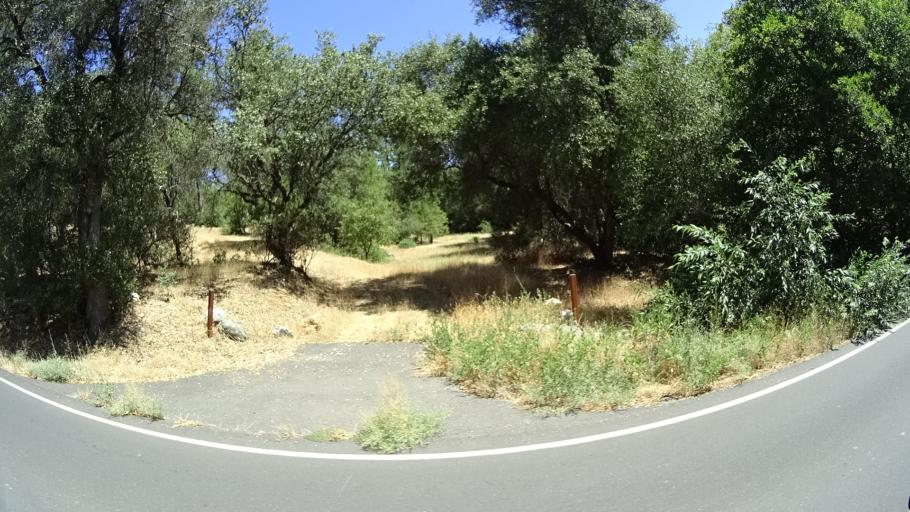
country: US
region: California
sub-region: Calaveras County
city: Murphys
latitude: 38.1297
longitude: -120.4441
